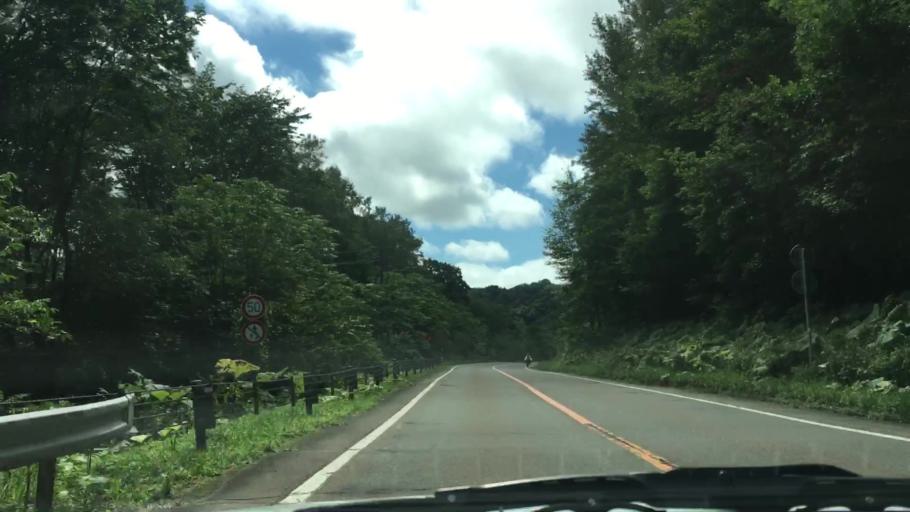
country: JP
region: Hokkaido
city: Kitami
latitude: 43.3495
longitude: 143.7771
